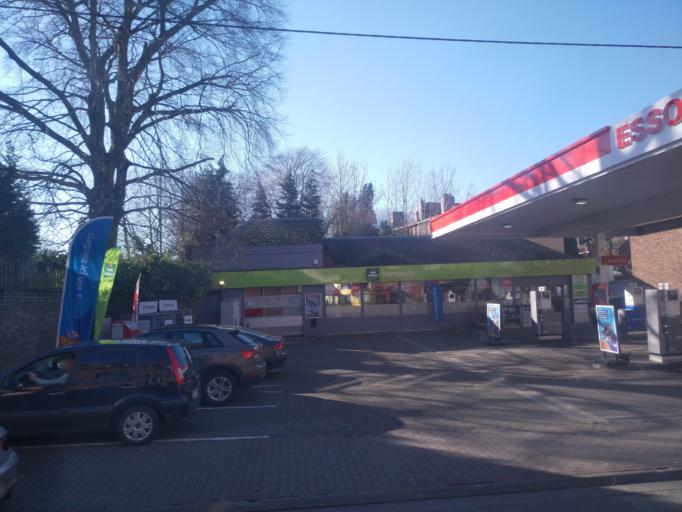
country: BE
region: Wallonia
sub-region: Province du Hainaut
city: Charleroi
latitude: 50.4017
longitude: 4.4454
